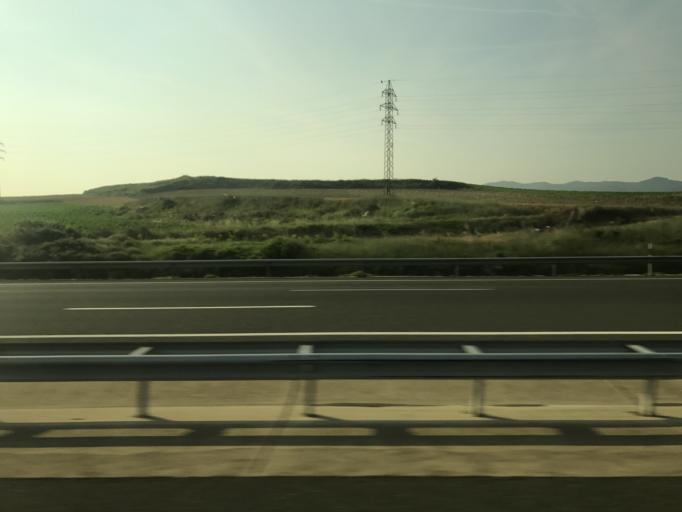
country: ES
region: Castille and Leon
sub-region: Provincia de Burgos
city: Miranda de Ebro
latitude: 42.6966
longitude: -2.9806
